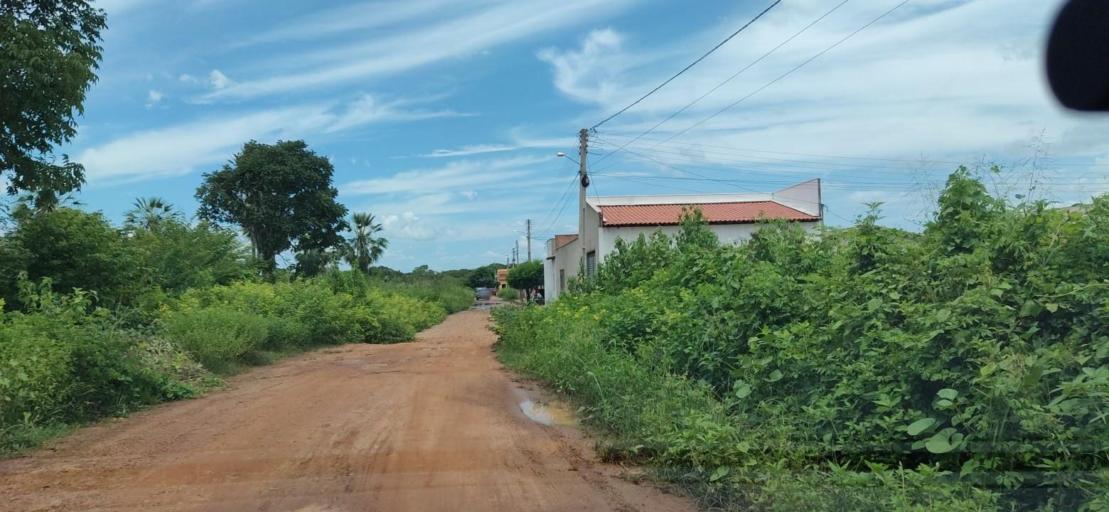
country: BR
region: Piaui
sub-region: Valenca Do Piaui
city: Valenca do Piaui
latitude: -6.4163
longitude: -41.7300
